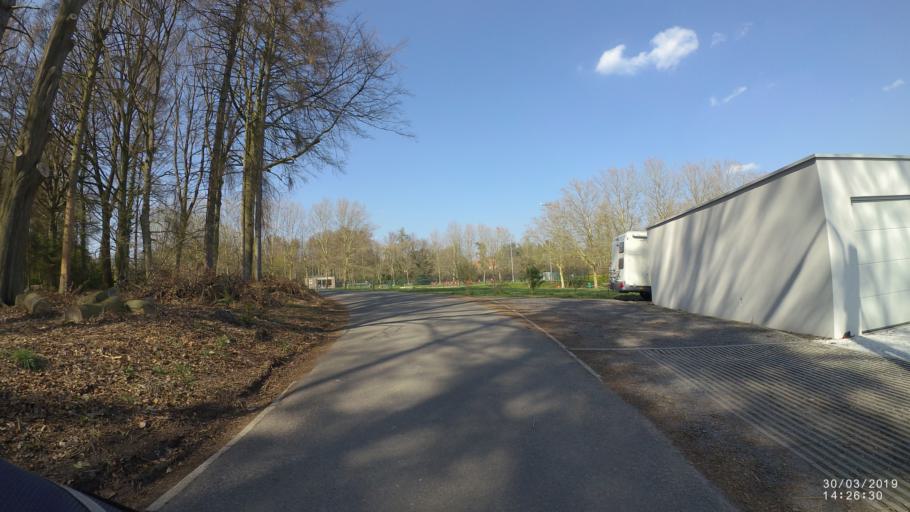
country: BE
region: Wallonia
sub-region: Province du Brabant Wallon
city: Wavre
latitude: 50.7143
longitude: 4.5777
